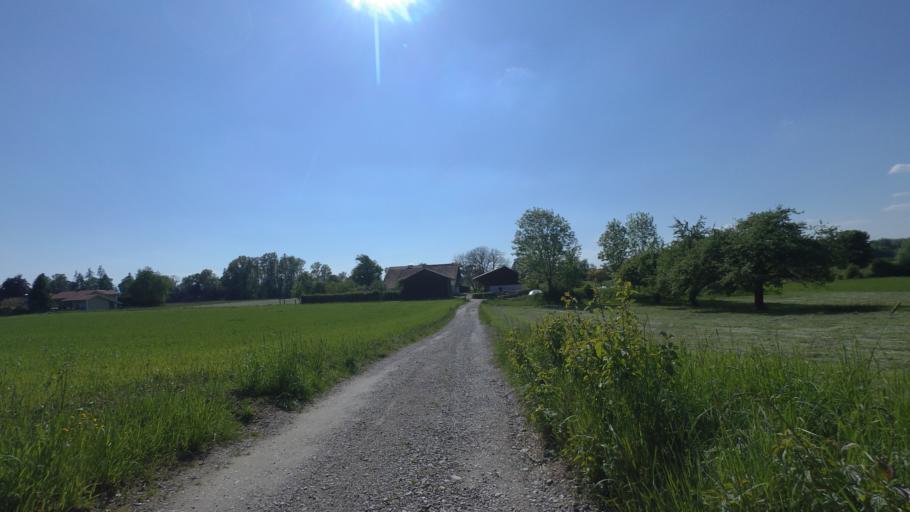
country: DE
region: Bavaria
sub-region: Upper Bavaria
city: Seeon-Seebruck
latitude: 47.9258
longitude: 12.4973
